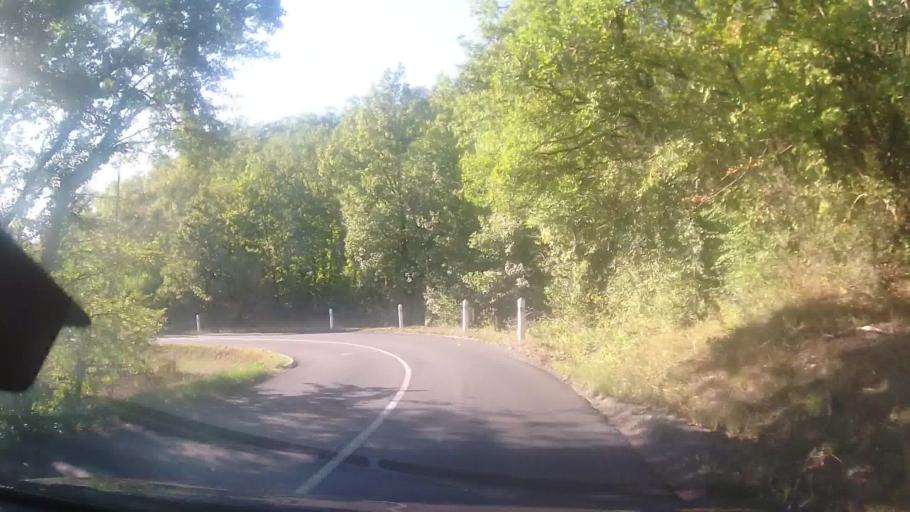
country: FR
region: Aquitaine
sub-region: Departement de la Dordogne
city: Cenac-et-Saint-Julien
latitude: 44.7888
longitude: 1.1775
